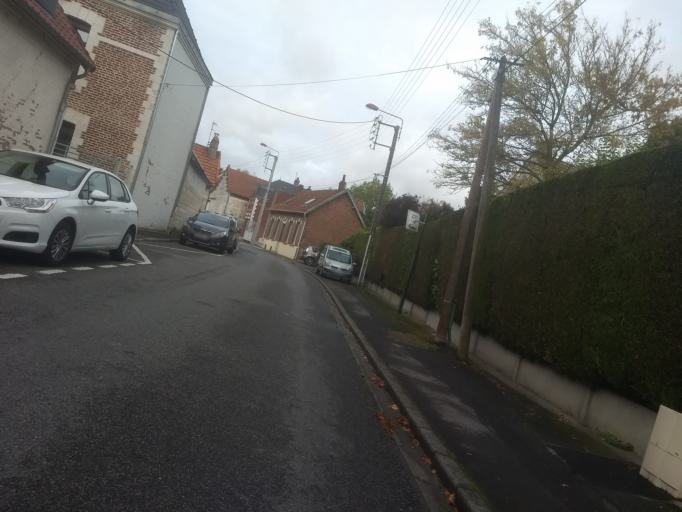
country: FR
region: Nord-Pas-de-Calais
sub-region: Departement du Pas-de-Calais
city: Anzin-Saint-Aubin
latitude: 50.3108
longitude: 2.7476
